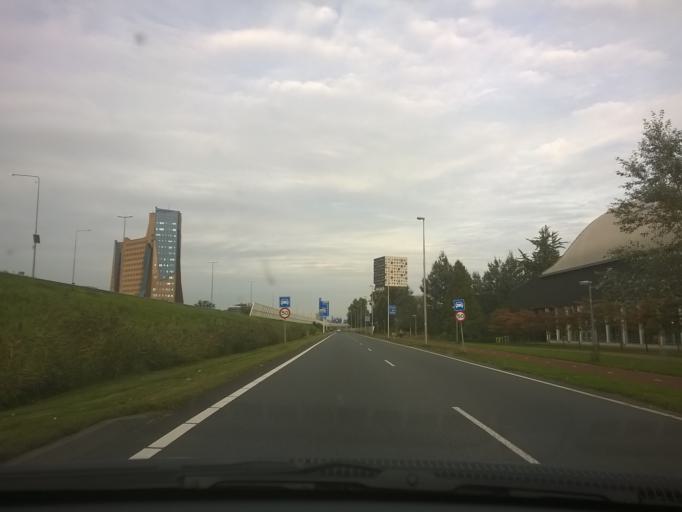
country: NL
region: Groningen
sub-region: Gemeente Groningen
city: Groningen
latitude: 53.1986
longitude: 6.5480
